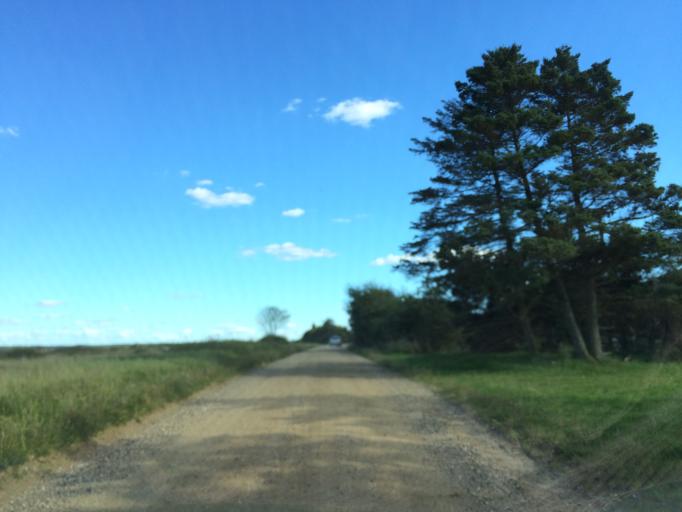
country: DK
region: Central Jutland
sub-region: Holstebro Kommune
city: Holstebro
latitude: 56.2767
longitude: 8.4912
